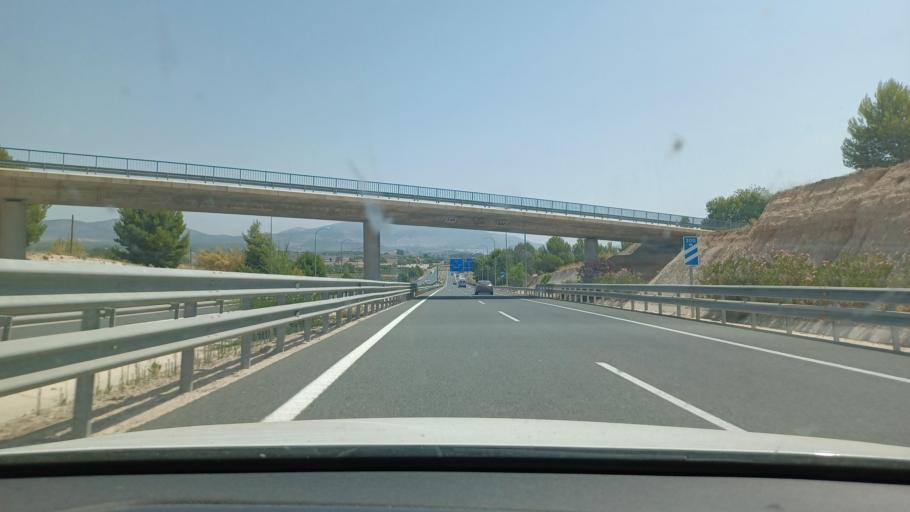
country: ES
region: Valencia
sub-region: Provincia de Alicante
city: Castalla
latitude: 38.5876
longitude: -0.6460
